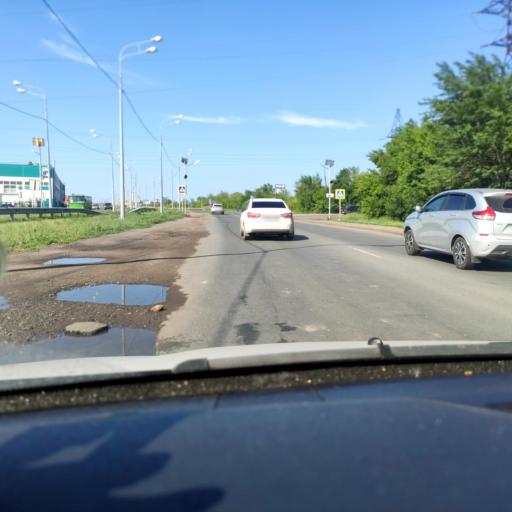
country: RU
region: Samara
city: Smyshlyayevka
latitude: 53.2648
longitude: 50.3904
